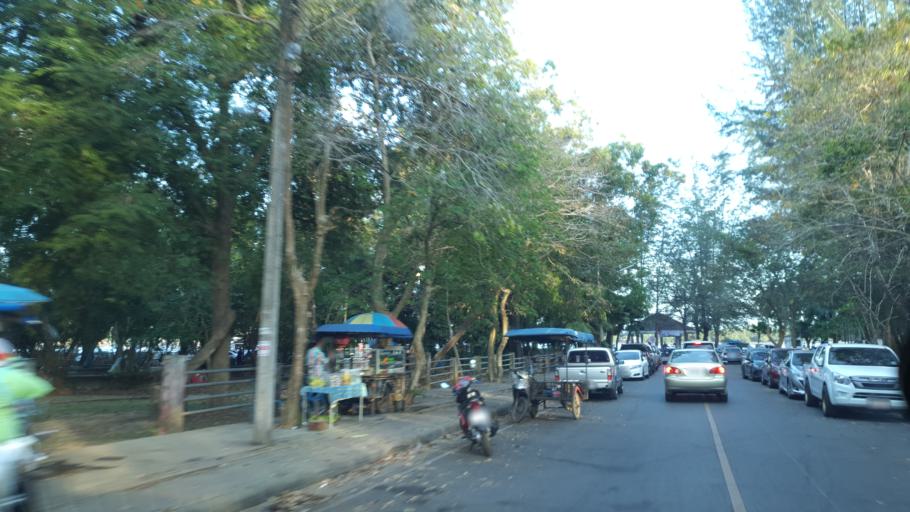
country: TH
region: Krabi
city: Krabi
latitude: 8.0531
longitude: 98.9189
